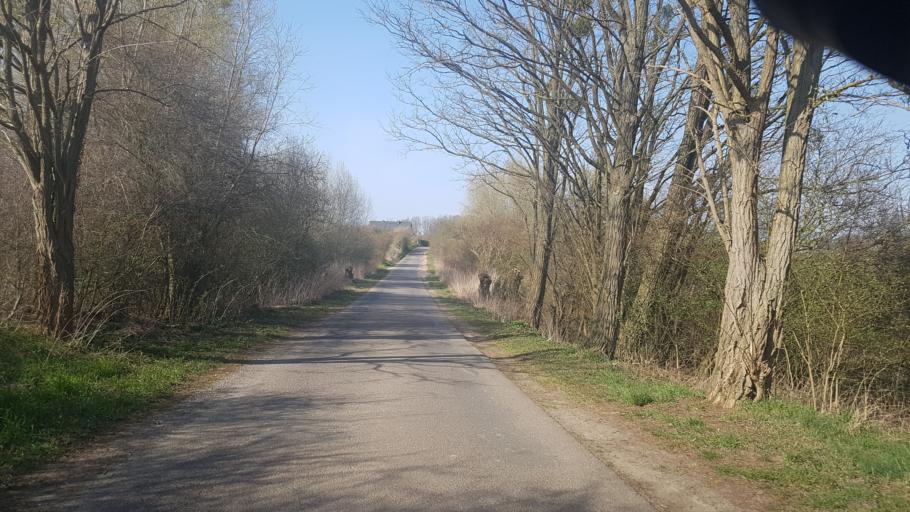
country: DE
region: Brandenburg
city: Gerswalde
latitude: 53.2017
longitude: 13.7824
